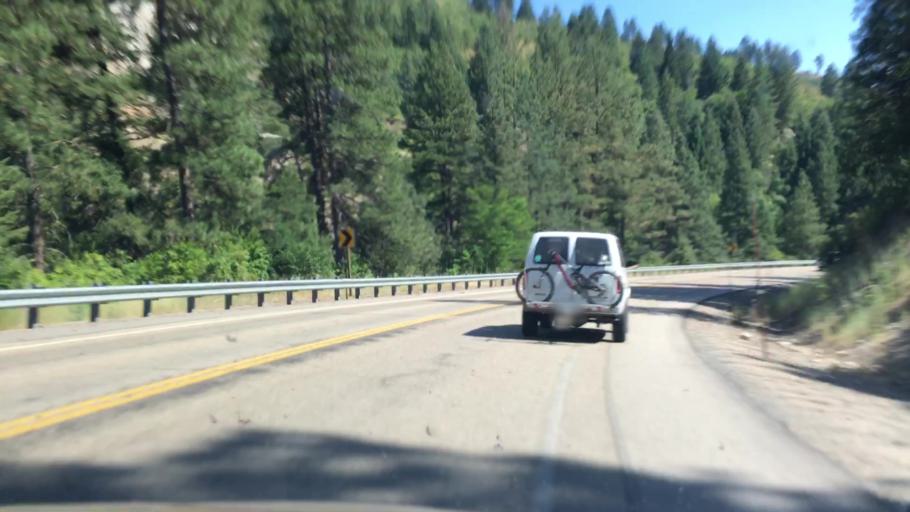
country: US
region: Idaho
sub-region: Valley County
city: Cascade
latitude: 44.1298
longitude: -116.1114
